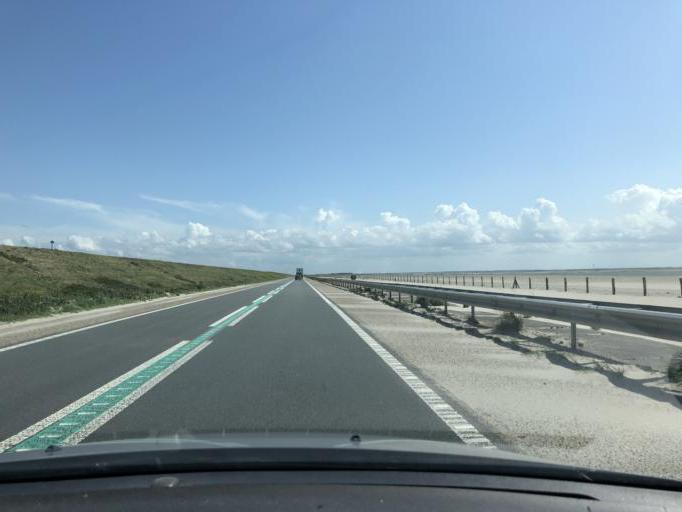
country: NL
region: North Holland
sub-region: Gemeente Enkhuizen
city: Enkhuizen
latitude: 52.6617
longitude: 5.3798
